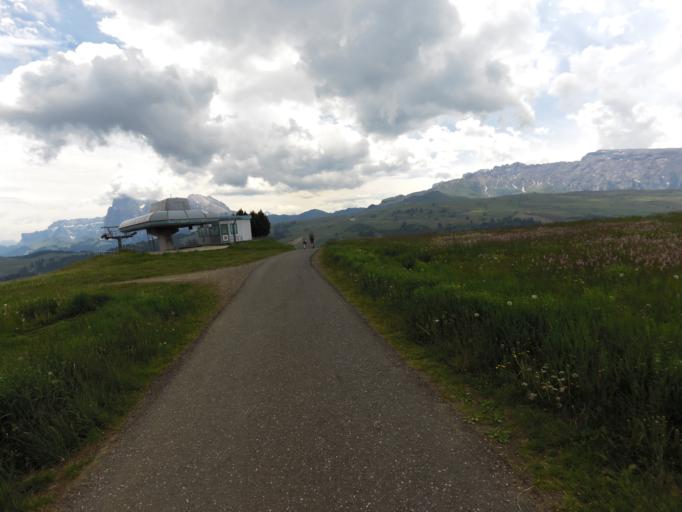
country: IT
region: Trentino-Alto Adige
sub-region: Bolzano
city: Siusi
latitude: 46.5448
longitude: 11.6136
